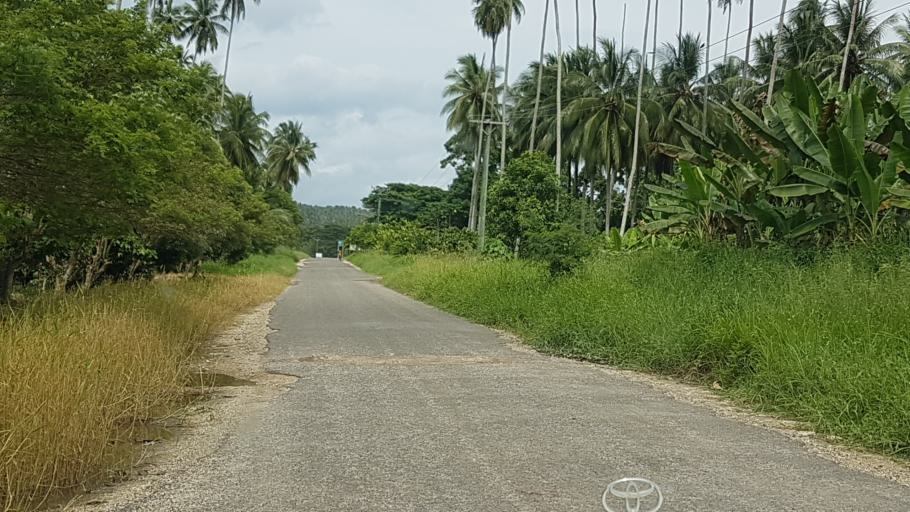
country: PG
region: Madang
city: Madang
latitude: -4.7942
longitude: 145.7242
